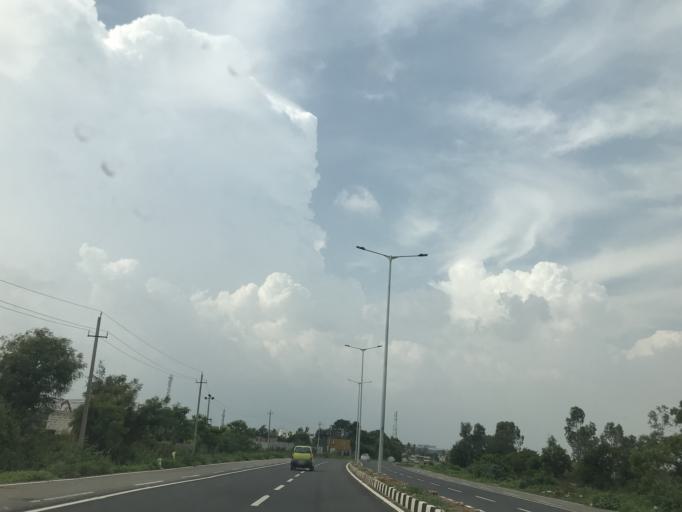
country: IN
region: Karnataka
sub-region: Bangalore Rural
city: Devanhalli
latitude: 13.1666
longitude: 77.6877
